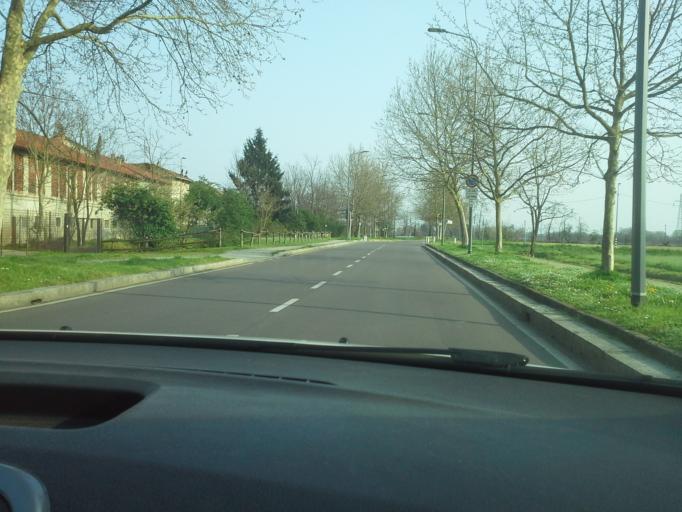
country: IT
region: Lombardy
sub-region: Citta metropolitana di Milano
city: Trezzano sul Naviglio
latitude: 45.4495
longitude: 9.0667
